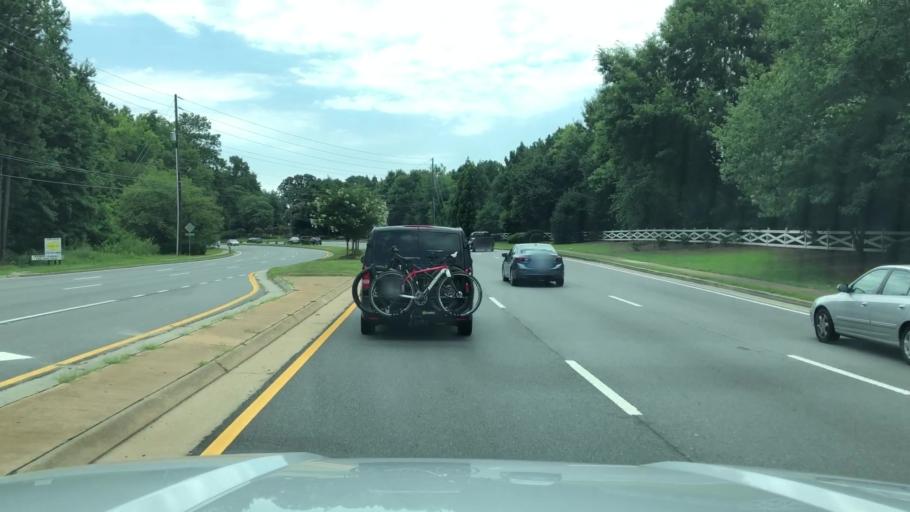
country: US
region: Georgia
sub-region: Fulton County
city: Roswell
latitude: 34.0551
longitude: -84.3772
